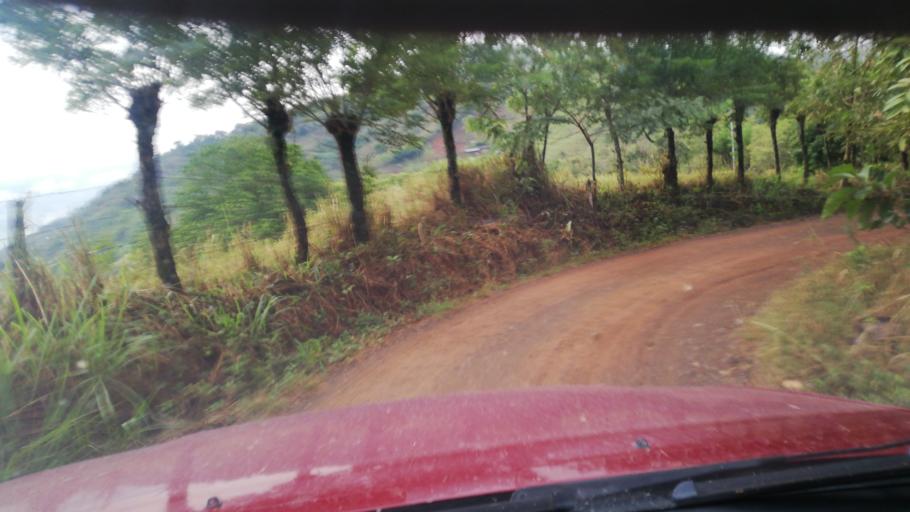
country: CO
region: Risaralda
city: La Virginia
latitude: 4.8818
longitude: -75.9488
